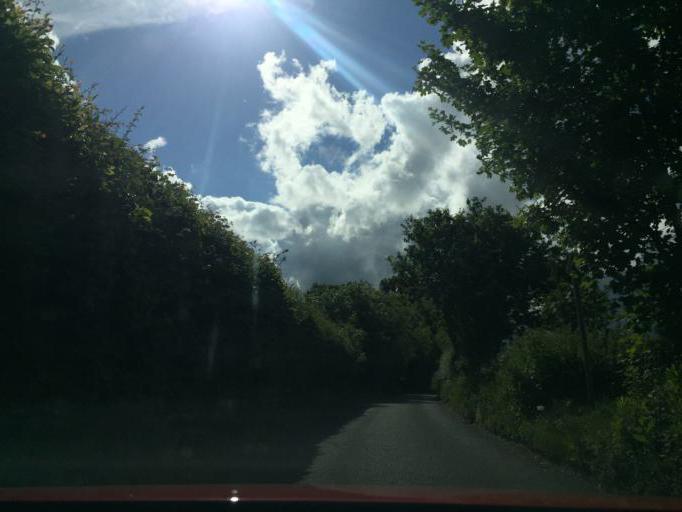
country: GB
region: England
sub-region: Hertfordshire
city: Wheathampstead
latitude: 51.8512
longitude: -0.3091
